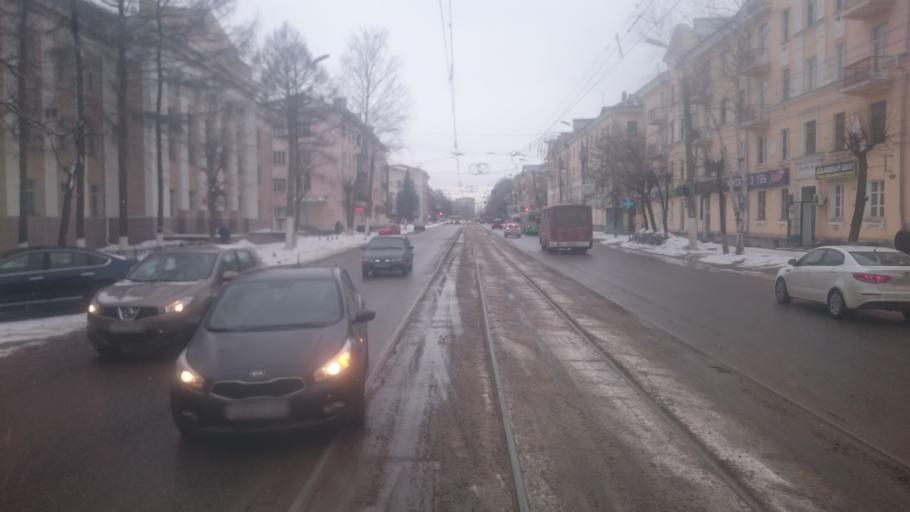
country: RU
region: Tverskaya
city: Tver
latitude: 56.8677
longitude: 35.9033
